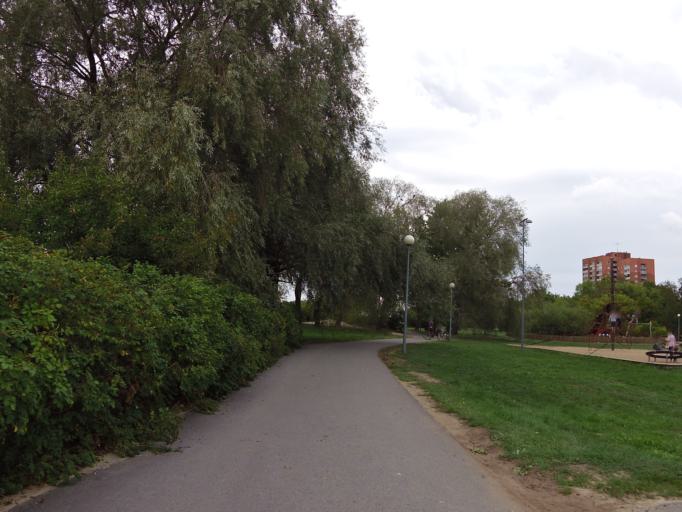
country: EE
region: Harju
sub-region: Tallinna linn
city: Tallinn
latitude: 59.4406
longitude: 24.6834
